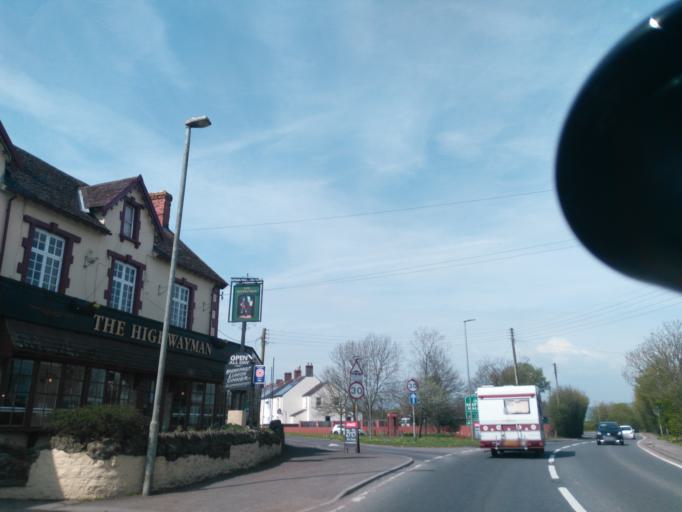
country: GB
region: England
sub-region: Somerset
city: Shepton Mallet
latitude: 51.1744
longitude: -2.5352
